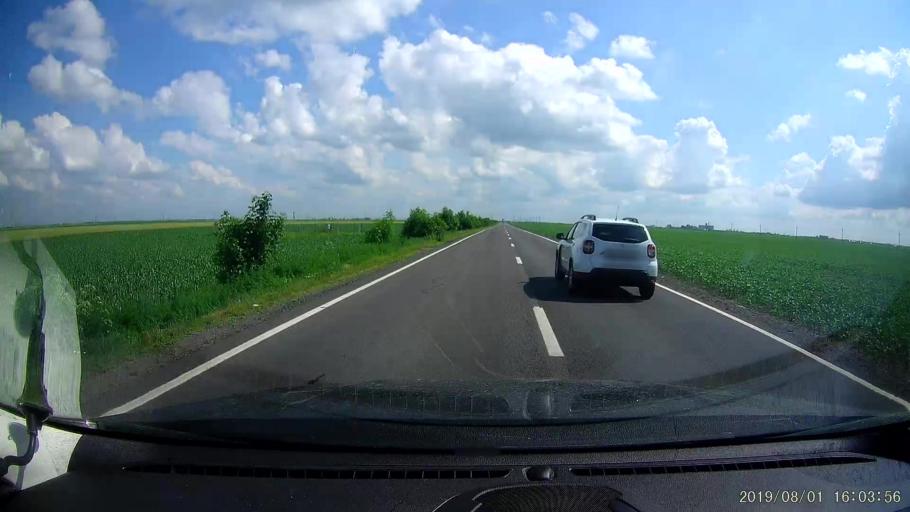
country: RO
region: Calarasi
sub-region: Comuna Dragalina
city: Drajna Noua
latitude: 44.4601
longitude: 27.3823
